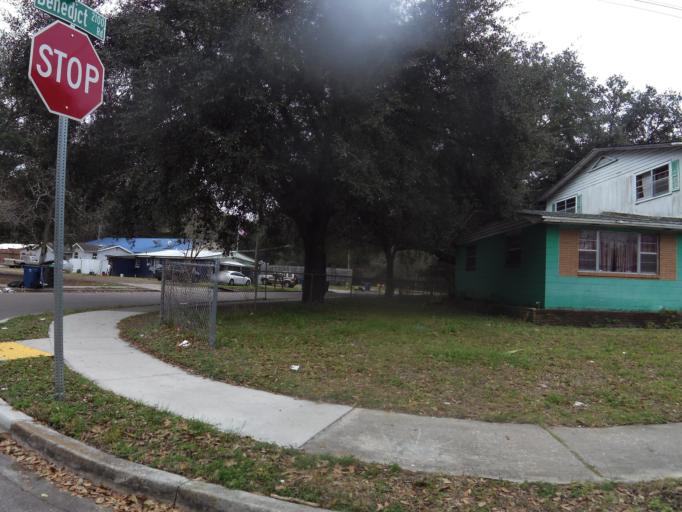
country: US
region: Florida
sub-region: Duval County
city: Jacksonville
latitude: 30.3781
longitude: -81.6982
